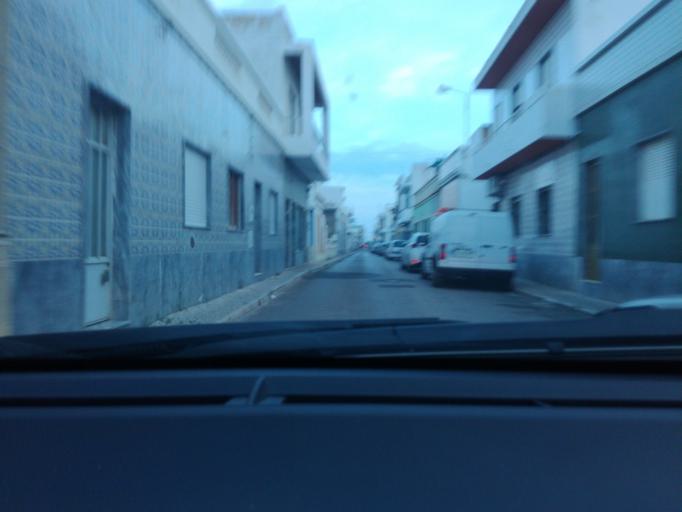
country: PT
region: Faro
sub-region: Olhao
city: Laranjeiro
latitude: 37.0574
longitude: -7.7484
